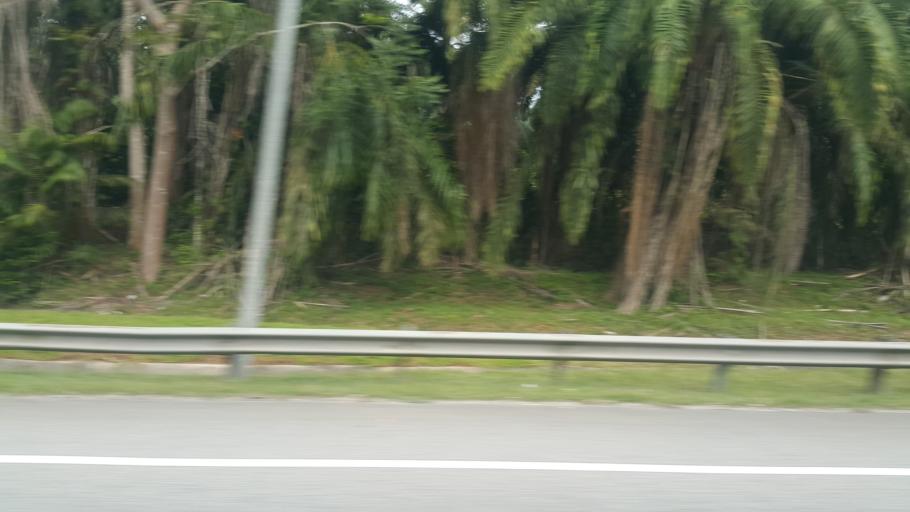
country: MY
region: Johor
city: Pekan Nenas
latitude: 1.4087
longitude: 103.5932
